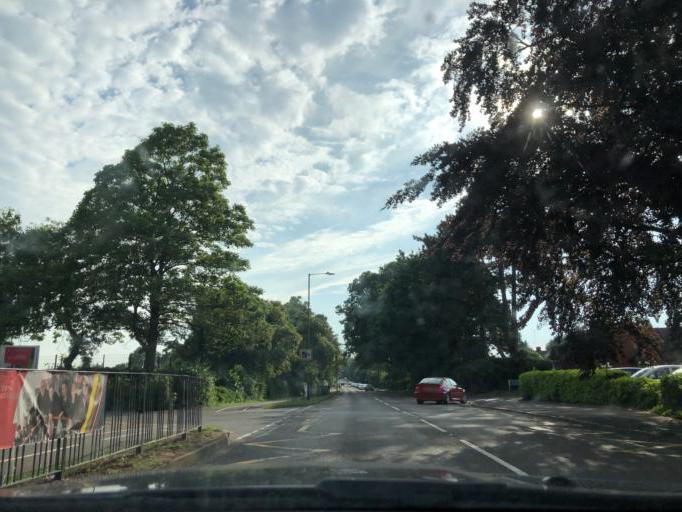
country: GB
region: England
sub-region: Warwickshire
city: Warwick
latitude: 52.2809
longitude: -1.5664
